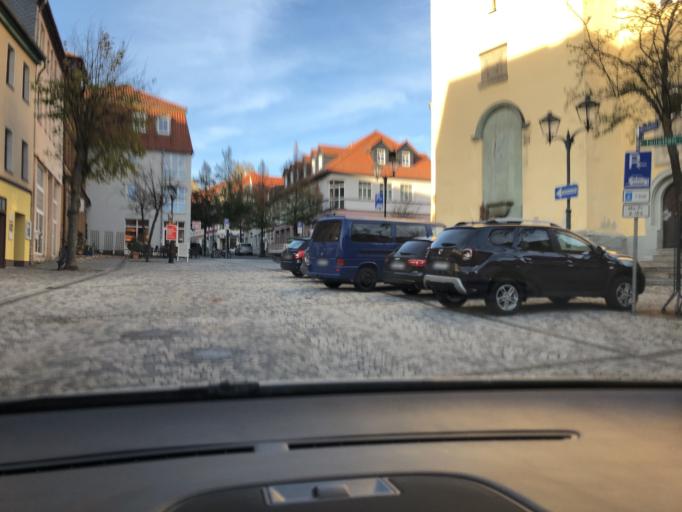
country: DE
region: Thuringia
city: Ilmenau
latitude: 50.6854
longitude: 10.9147
